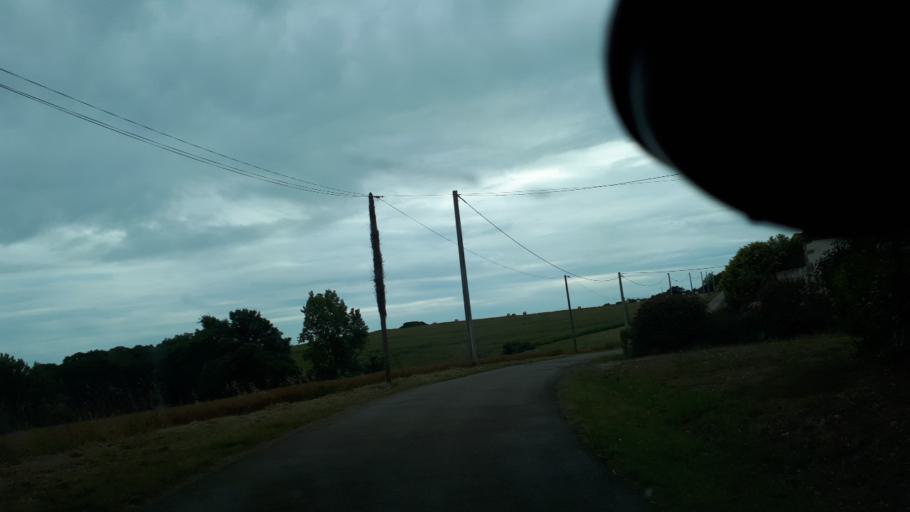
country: FR
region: Brittany
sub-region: Departement du Finistere
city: Plozevet
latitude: 47.9699
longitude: -4.3896
